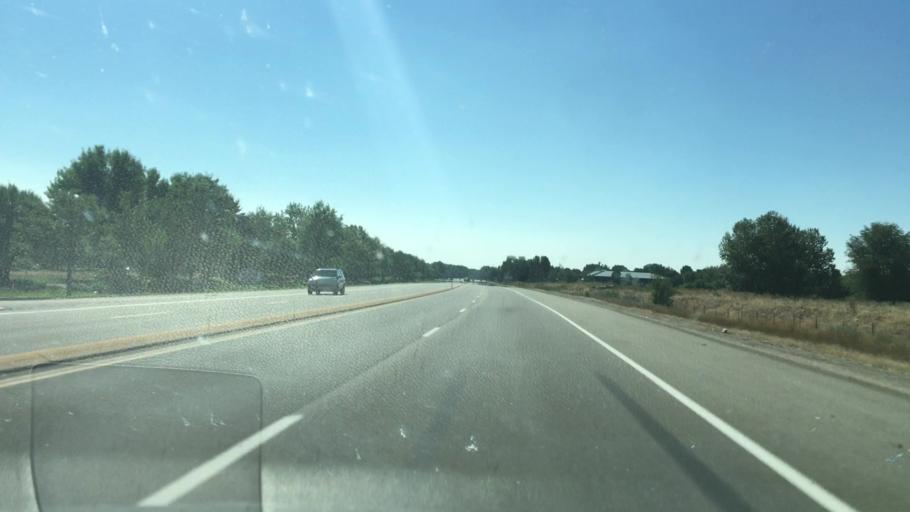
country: US
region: Idaho
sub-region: Ada County
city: Eagle
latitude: 43.6900
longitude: -116.3439
